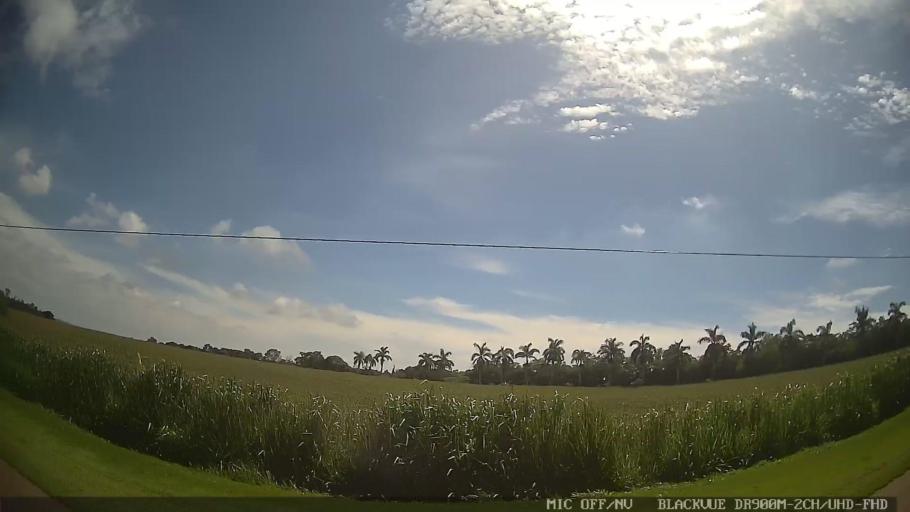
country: BR
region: Sao Paulo
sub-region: Tiete
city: Tiete
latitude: -23.1308
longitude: -47.6943
